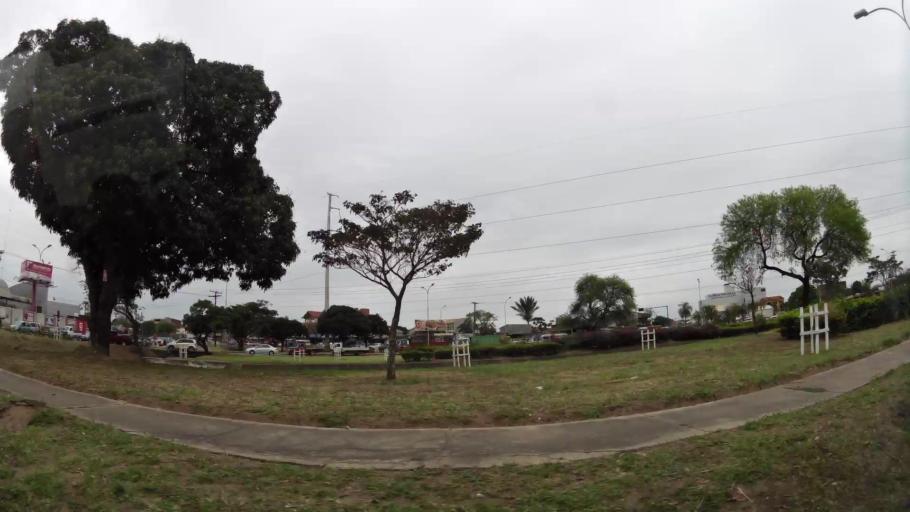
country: BO
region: Santa Cruz
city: Santa Cruz de la Sierra
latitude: -17.7562
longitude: -63.1546
